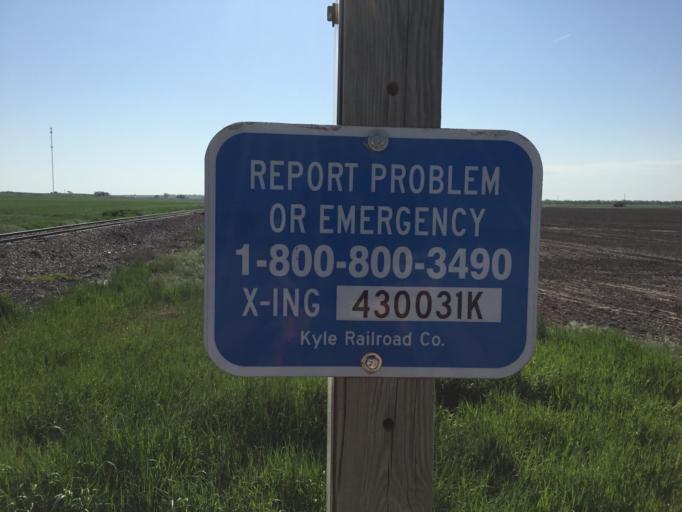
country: US
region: Kansas
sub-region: Mitchell County
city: Beloit
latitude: 39.4536
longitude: -98.0785
